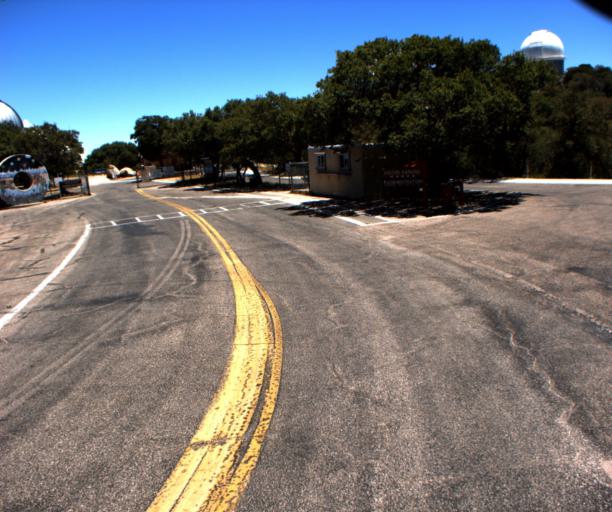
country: US
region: Arizona
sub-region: Pima County
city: Sells
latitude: 31.9604
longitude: -111.5988
